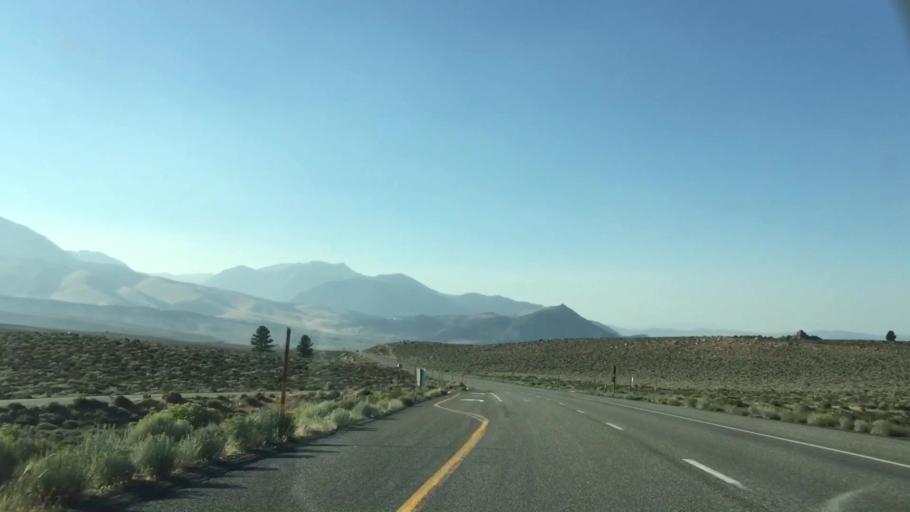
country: US
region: California
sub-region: Mono County
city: Mammoth Lakes
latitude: 37.8416
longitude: -119.0716
